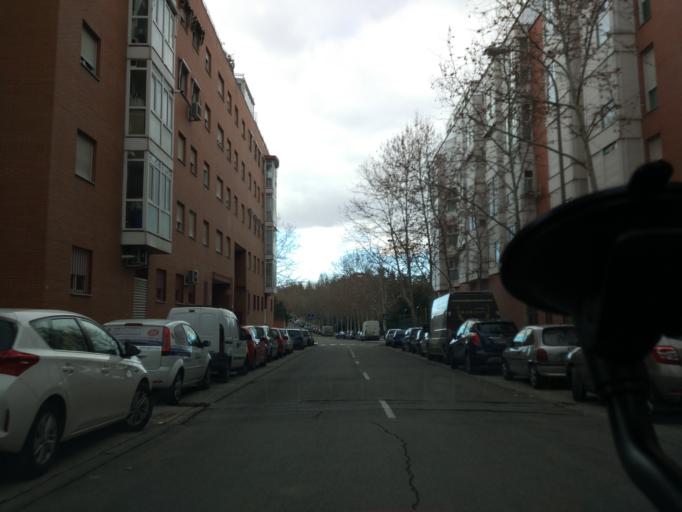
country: ES
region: Madrid
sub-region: Provincia de Madrid
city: San Blas
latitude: 40.4410
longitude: -3.6293
